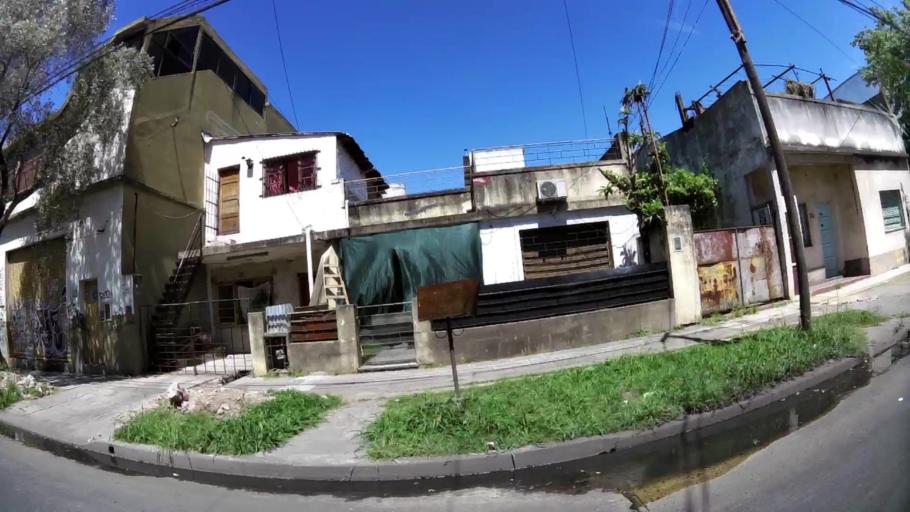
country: AR
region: Buenos Aires
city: Caseros
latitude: -34.5762
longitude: -58.5642
